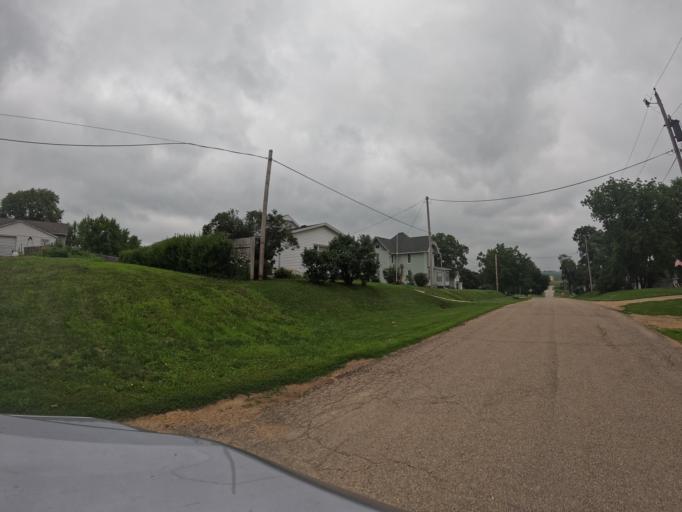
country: US
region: Iowa
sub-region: Clinton County
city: De Witt
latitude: 41.9127
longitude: -90.6034
